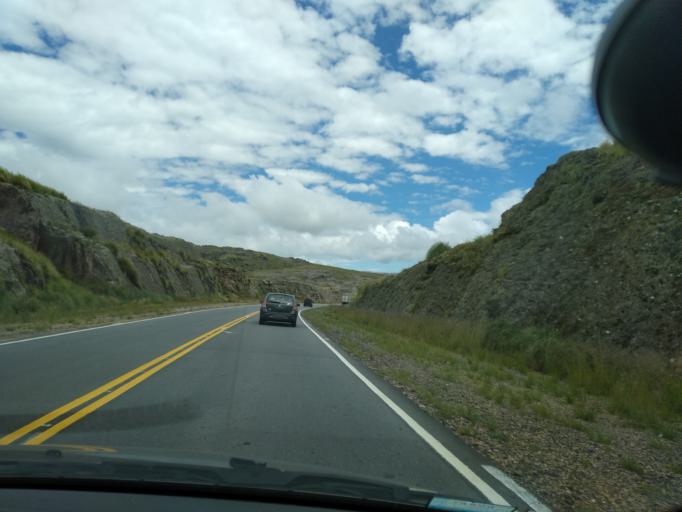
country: AR
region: Cordoba
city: Cuesta Blanca
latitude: -31.6075
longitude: -64.7173
